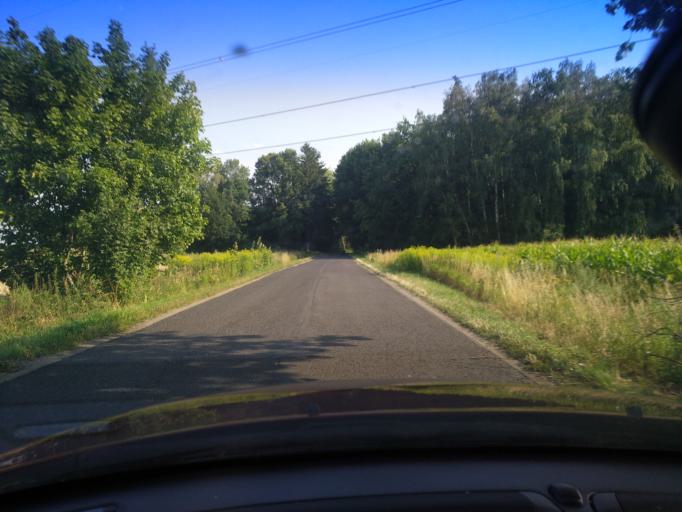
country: PL
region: Lower Silesian Voivodeship
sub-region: Powiat zgorzelecki
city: Sulikow
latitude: 51.0878
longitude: 15.0972
